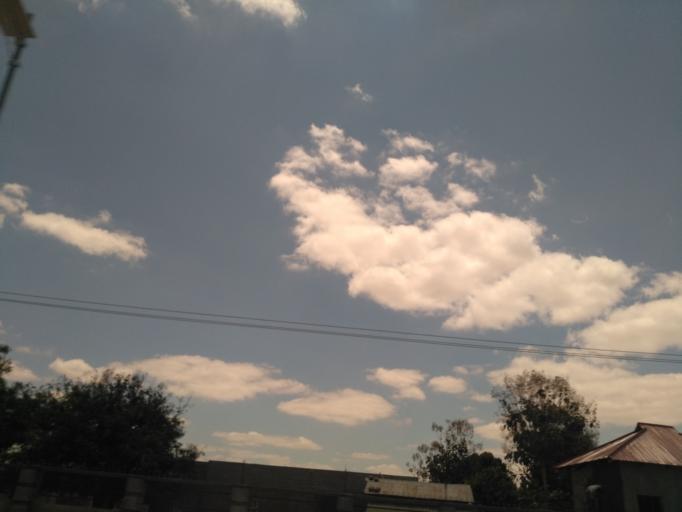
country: TZ
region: Dodoma
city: Kisasa
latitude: -6.1629
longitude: 35.7689
